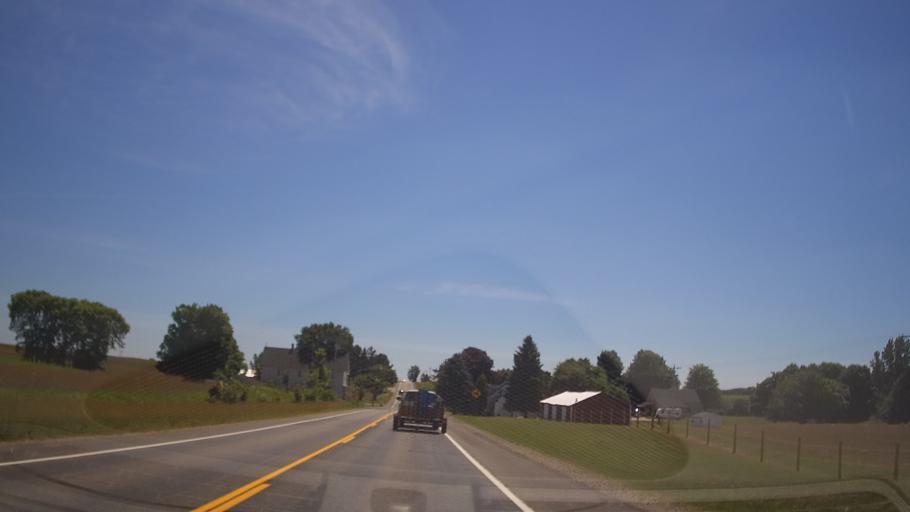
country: US
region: Michigan
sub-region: Grand Traverse County
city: Kingsley
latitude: 44.6156
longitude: -85.6966
